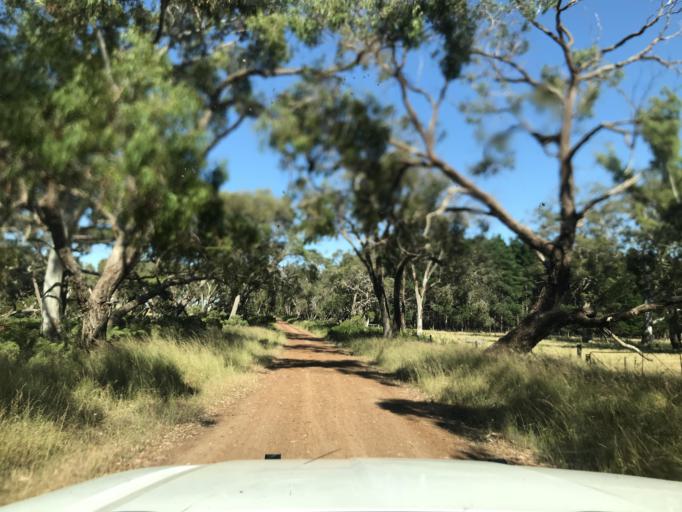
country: AU
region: South Australia
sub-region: Wattle Range
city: Penola
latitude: -37.0795
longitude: 141.3743
